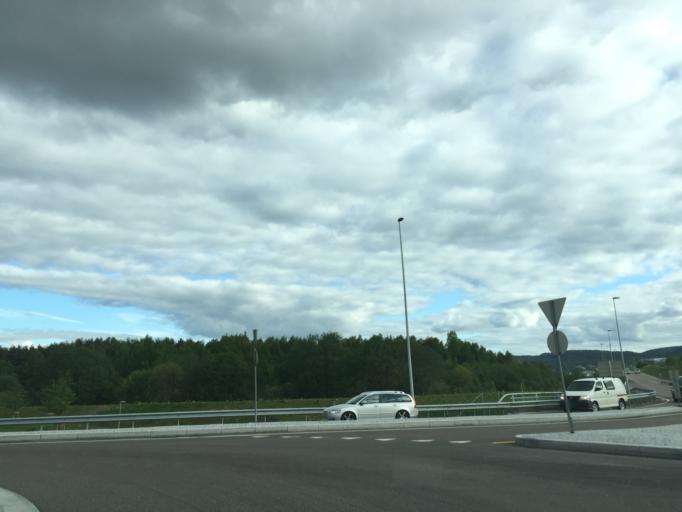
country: NO
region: Akershus
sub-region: Skedsmo
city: Lillestrom
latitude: 59.9530
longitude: 11.0774
